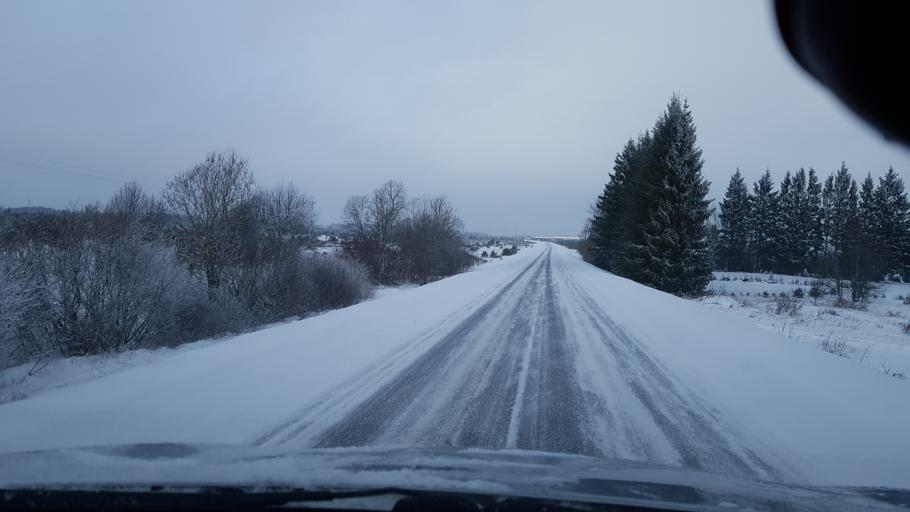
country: EE
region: Harju
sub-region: Keila linn
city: Keila
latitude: 59.3778
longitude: 24.4042
